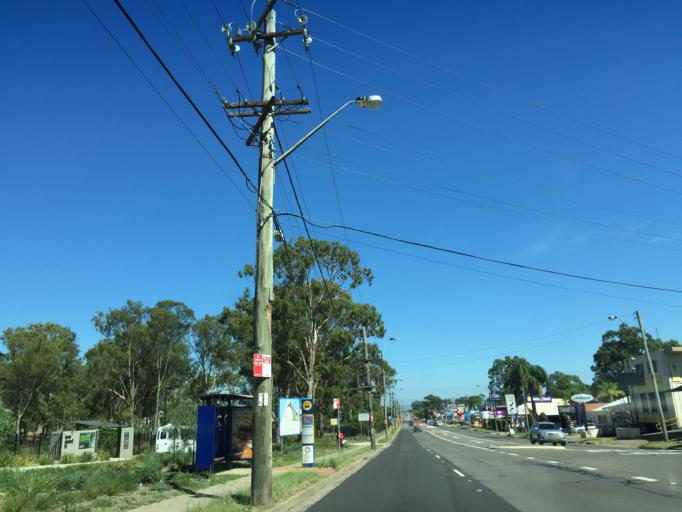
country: AU
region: New South Wales
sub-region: Blacktown
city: Blacktown
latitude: -33.7654
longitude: 150.9037
